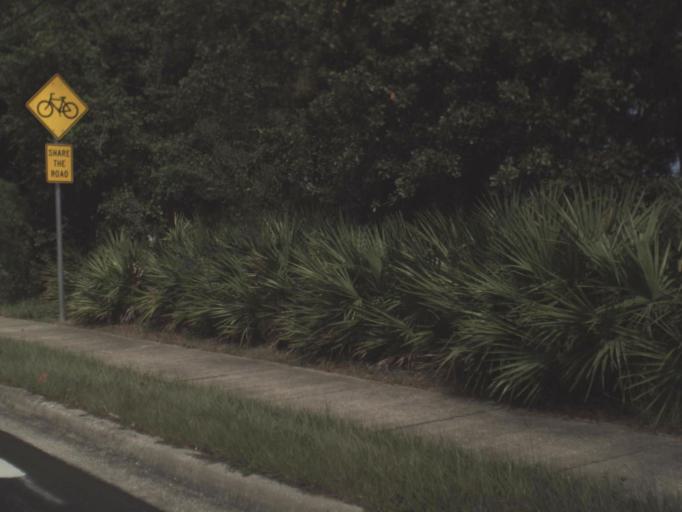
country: US
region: Florida
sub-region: Pinellas County
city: Safety Harbor
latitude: 28.0271
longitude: -82.7020
